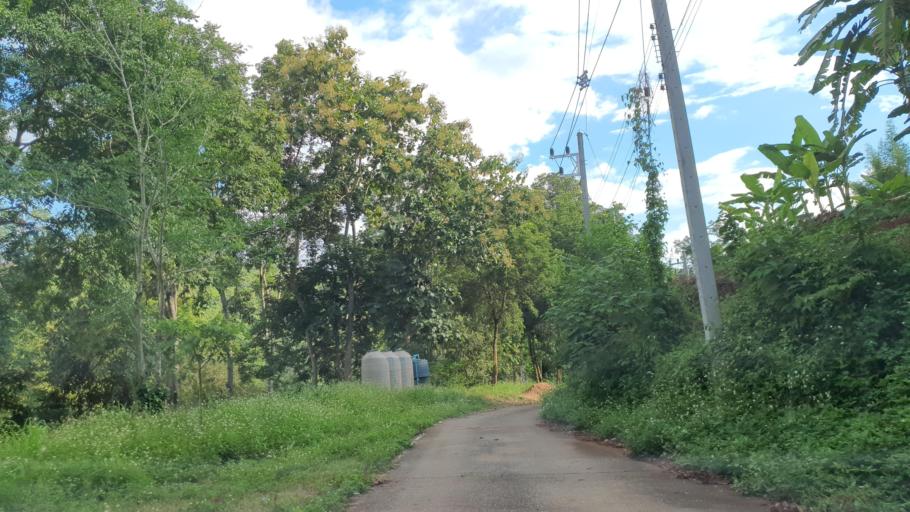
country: TH
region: Chiang Mai
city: Hang Dong
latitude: 18.7619
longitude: 98.8689
